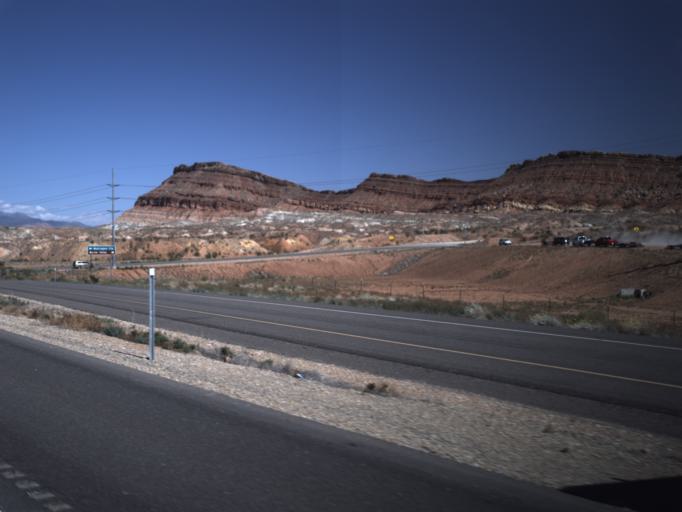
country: US
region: Utah
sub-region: Washington County
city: Washington
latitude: 37.0573
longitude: -113.4857
